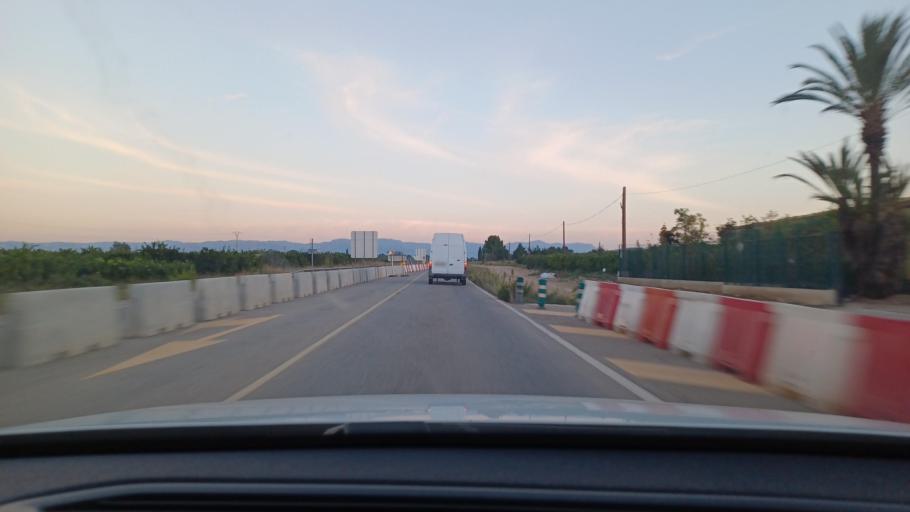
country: ES
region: Catalonia
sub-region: Provincia de Tarragona
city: Alcanar
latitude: 40.5490
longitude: 0.4342
